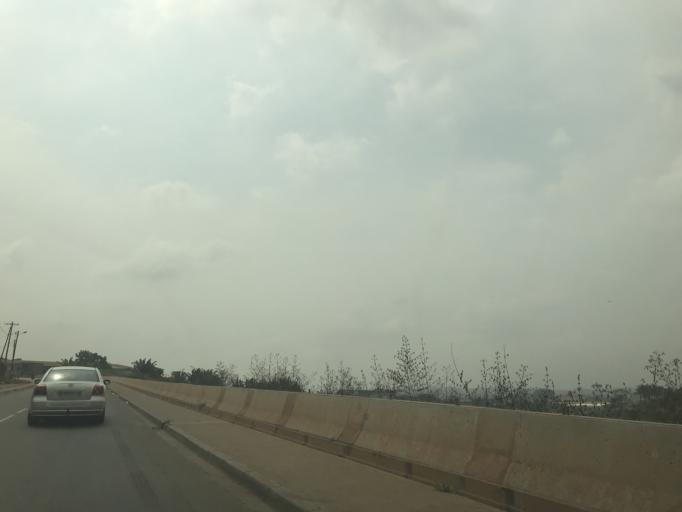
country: CM
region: Centre
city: Yaounde
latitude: 3.8229
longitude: 11.5131
